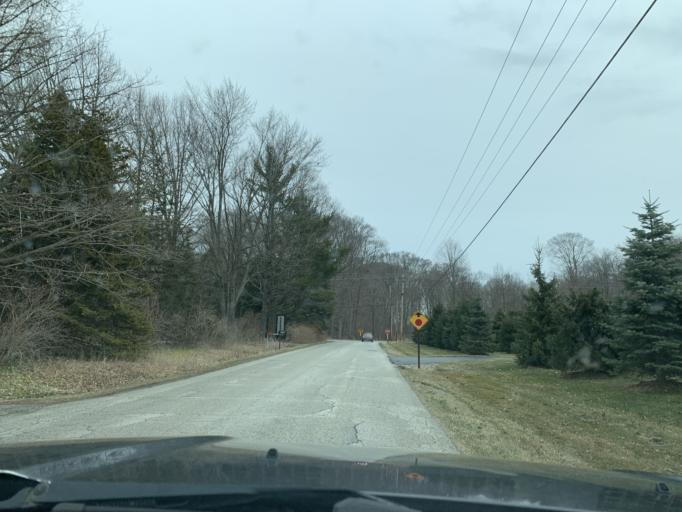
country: US
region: Indiana
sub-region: Porter County
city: Chesterton
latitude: 41.5855
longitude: -86.9909
